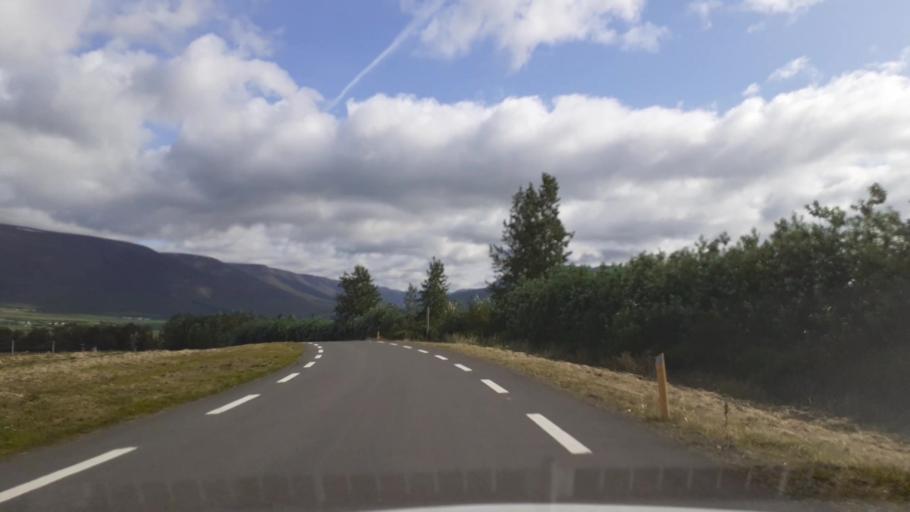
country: IS
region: Northeast
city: Akureyri
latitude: 65.6497
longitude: -18.0911
